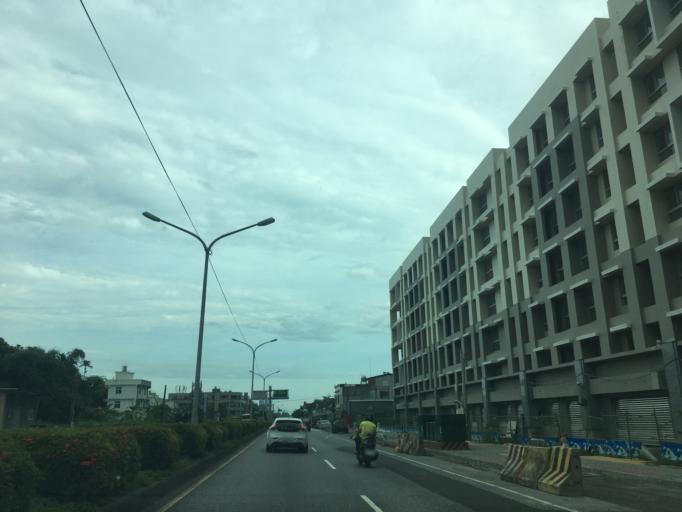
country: TW
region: Taiwan
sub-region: Hualien
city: Hualian
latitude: 24.0391
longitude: 121.6039
